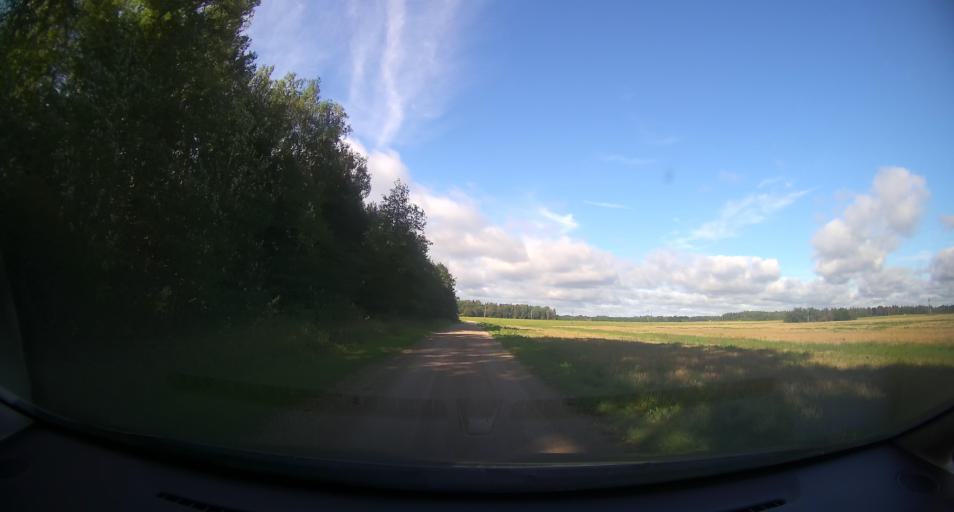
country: EE
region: Harju
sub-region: Raasiku vald
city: Raasiku
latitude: 59.2168
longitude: 25.2206
